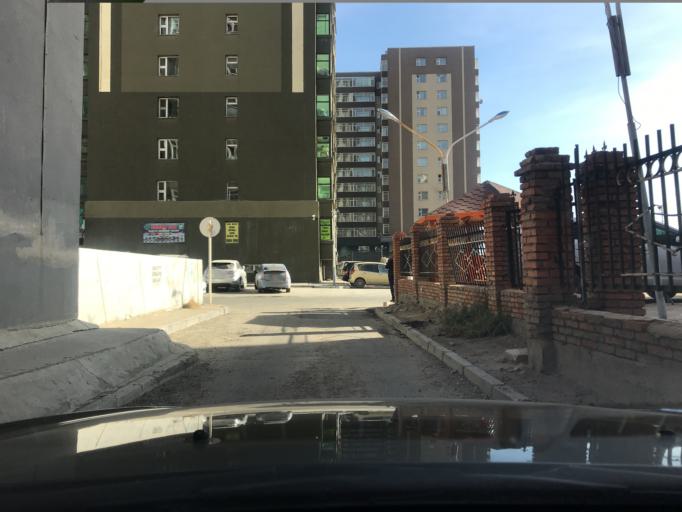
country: MN
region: Ulaanbaatar
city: Ulaanbaatar
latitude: 47.9088
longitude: 106.9412
